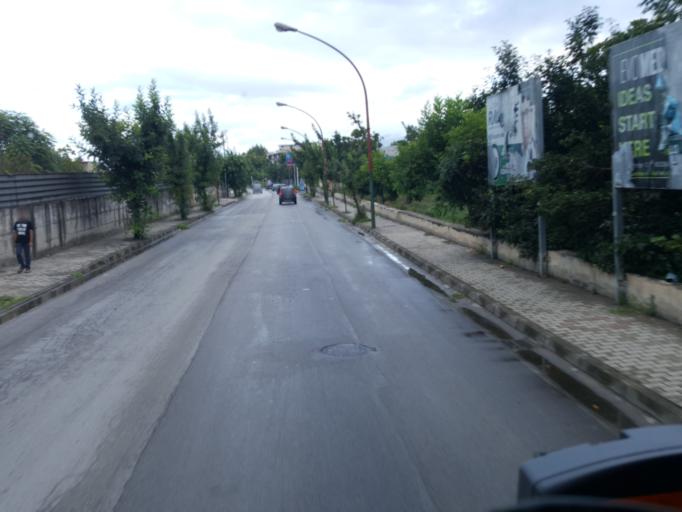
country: IT
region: Campania
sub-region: Provincia di Napoli
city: Palma Campania
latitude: 40.8648
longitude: 14.5485
